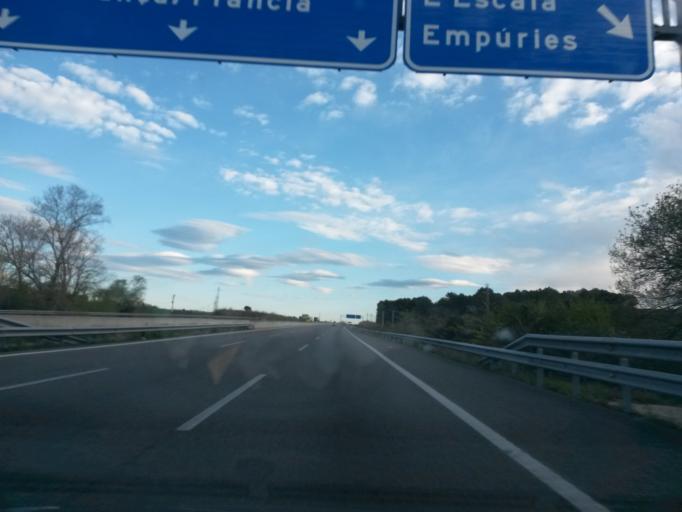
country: ES
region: Catalonia
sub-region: Provincia de Girona
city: Vilademuls
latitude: 42.1174
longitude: 2.9128
